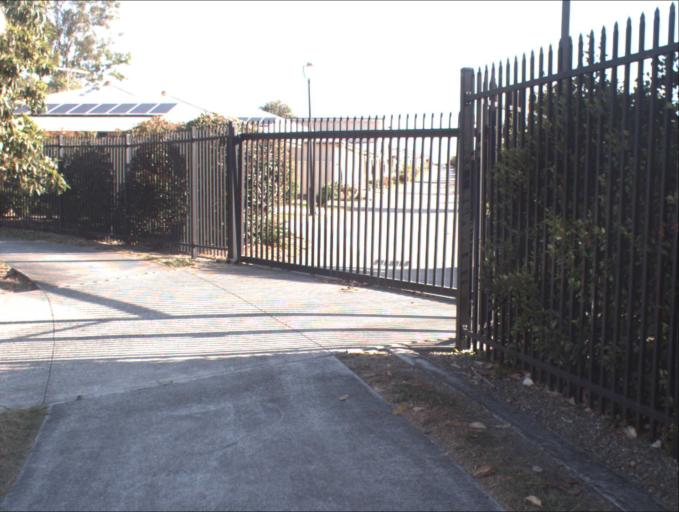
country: AU
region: Queensland
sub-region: Gold Coast
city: Yatala
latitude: -27.7073
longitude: 153.2202
